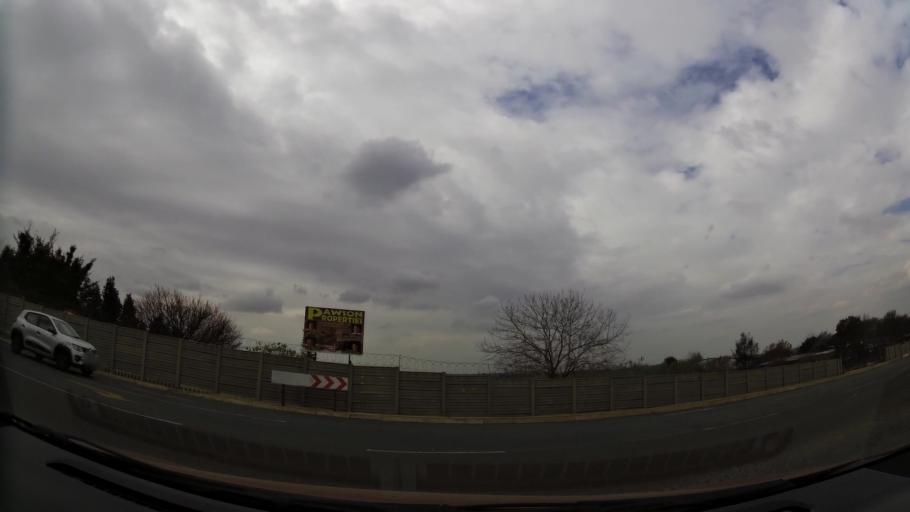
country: ZA
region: Gauteng
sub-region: West Rand District Municipality
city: Muldersdriseloop
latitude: -26.0925
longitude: 27.8742
